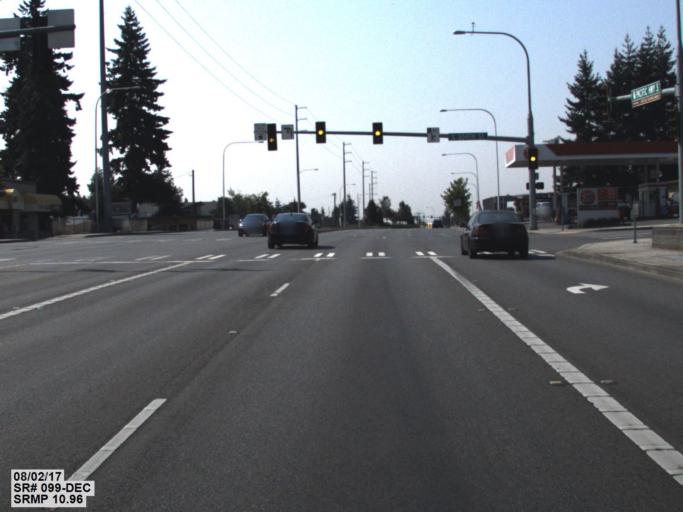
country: US
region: Washington
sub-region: King County
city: Federal Way
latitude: 47.3299
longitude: -122.3122
